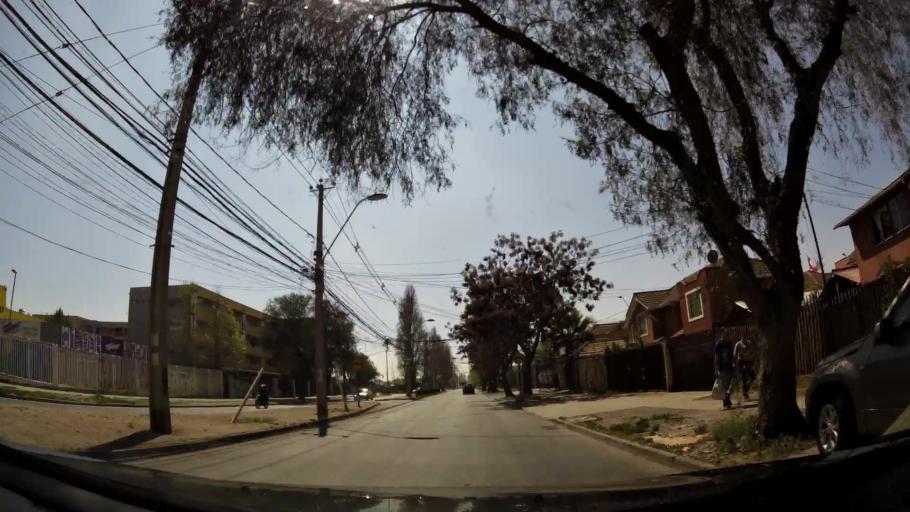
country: CL
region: Santiago Metropolitan
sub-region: Provincia de Santiago
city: Lo Prado
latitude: -33.3584
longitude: -70.7208
